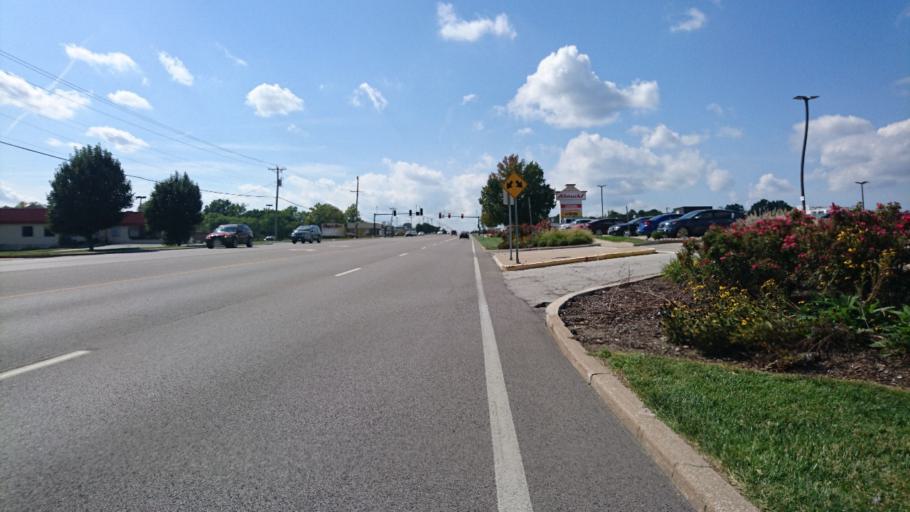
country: US
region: Missouri
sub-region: Saint Louis County
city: Ballwin
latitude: 38.5929
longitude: -90.5628
